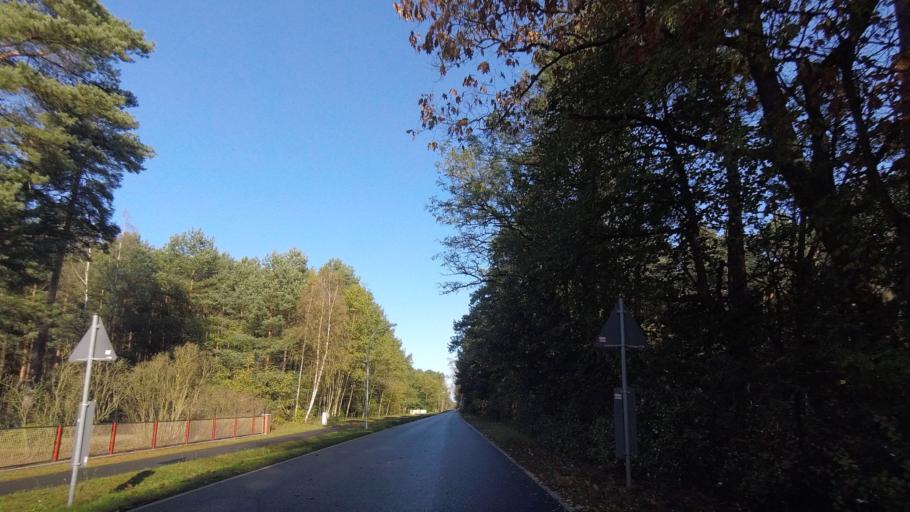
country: DE
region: Brandenburg
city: Borkheide
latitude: 52.2334
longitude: 12.8546
